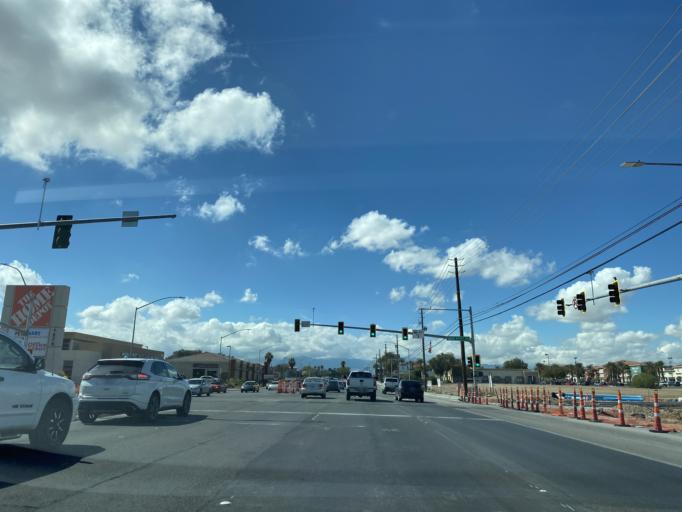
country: US
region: Nevada
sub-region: Clark County
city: North Las Vegas
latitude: 36.2395
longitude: -115.1566
